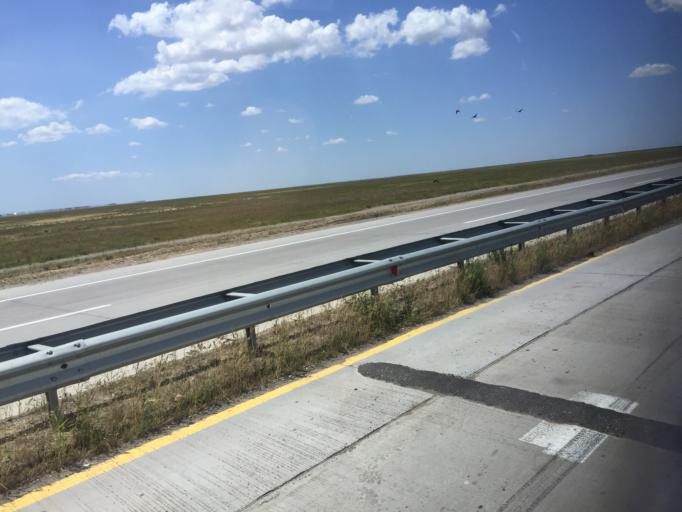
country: KZ
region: Ongtustik Qazaqstan
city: Temirlanovka
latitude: 42.8145
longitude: 69.1636
